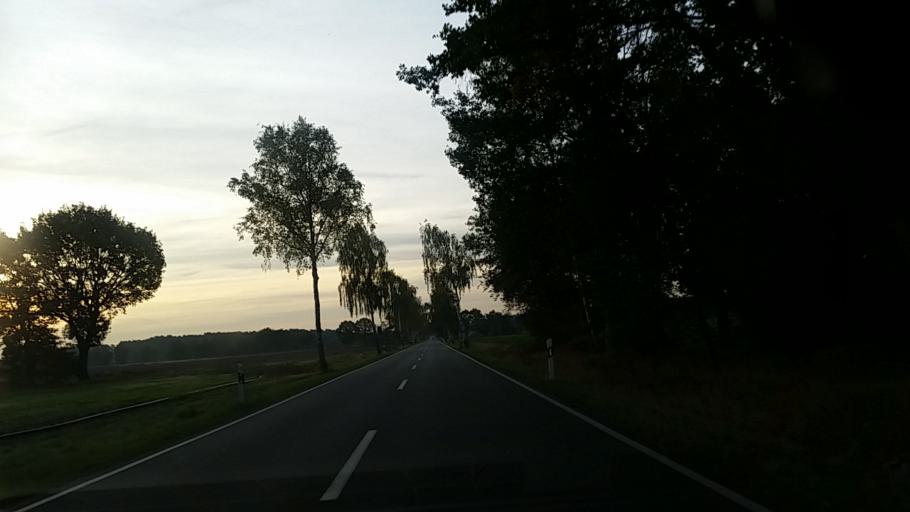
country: DE
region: Lower Saxony
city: Tiddische
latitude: 52.4929
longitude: 10.8027
